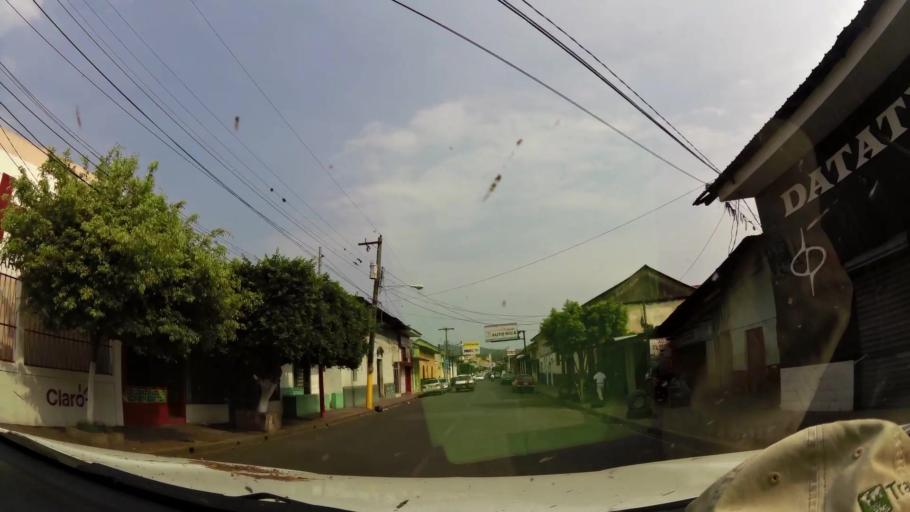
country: NI
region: Masaya
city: Masaya
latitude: 11.9720
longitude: -86.0954
